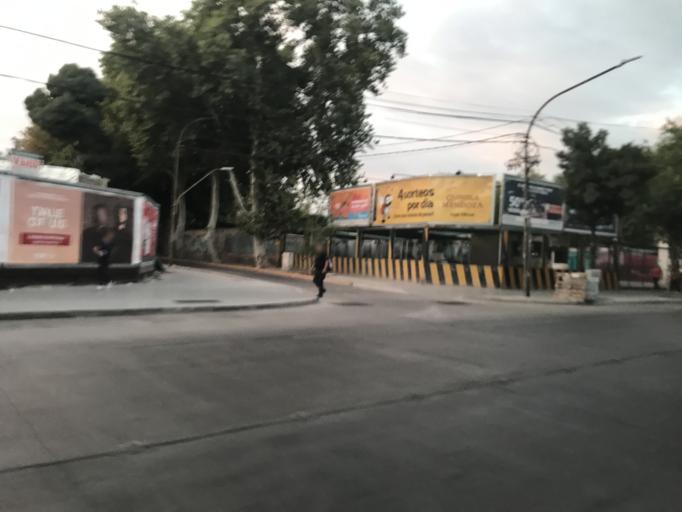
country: AR
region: Mendoza
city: Mendoza
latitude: -32.8929
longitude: -68.8353
